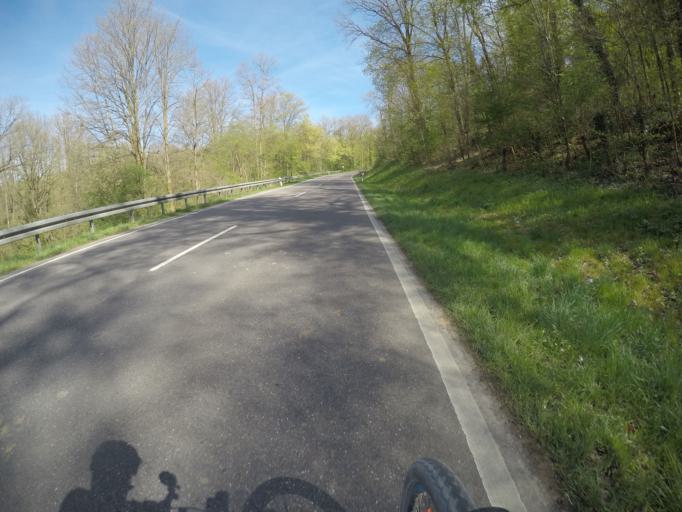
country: DE
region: Baden-Wuerttemberg
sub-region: Regierungsbezirk Stuttgart
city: Hemmingen
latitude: 48.8579
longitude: 9.0549
